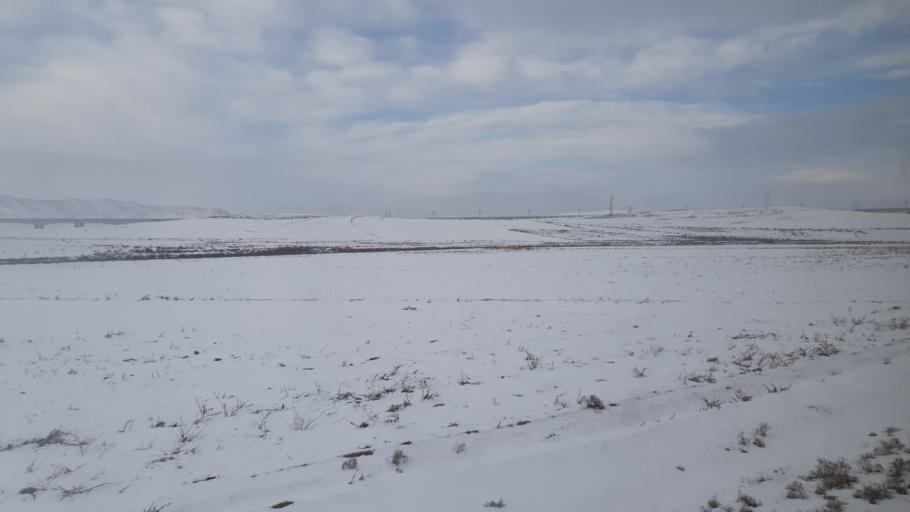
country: TR
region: Kirikkale
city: Delice
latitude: 39.8967
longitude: 33.9839
